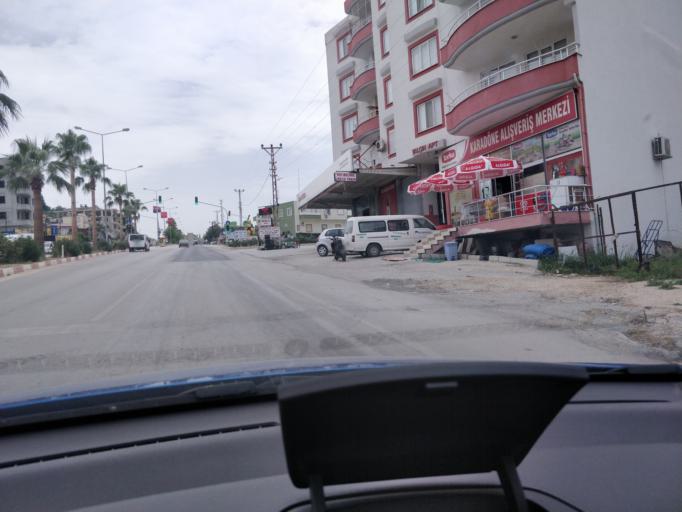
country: TR
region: Mersin
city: Mut
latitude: 36.6509
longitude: 33.4254
